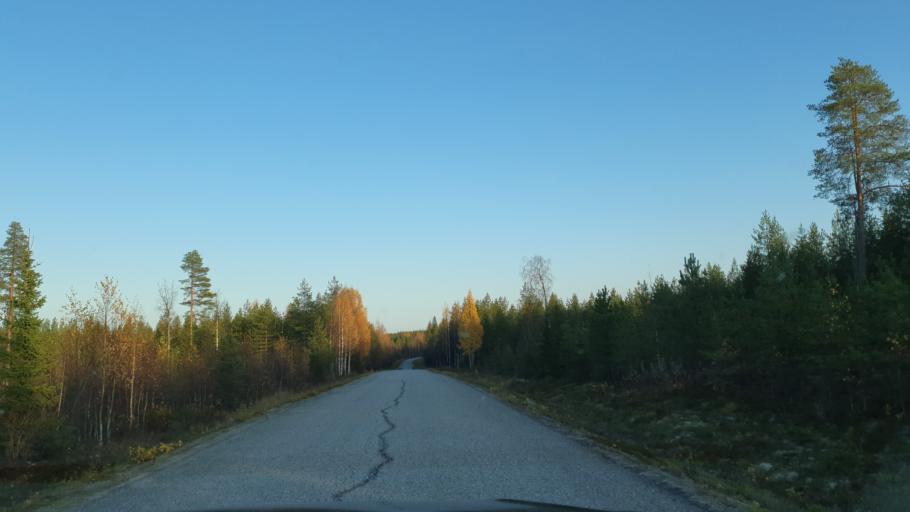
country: FI
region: Kainuu
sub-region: Kehys-Kainuu
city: Kuhmo
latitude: 64.4508
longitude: 29.6735
